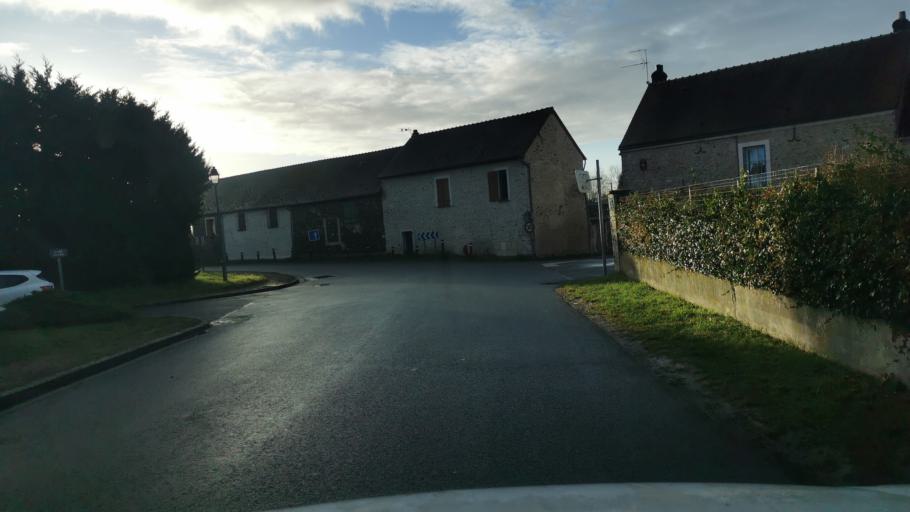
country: FR
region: Ile-de-France
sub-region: Departement des Yvelines
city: Bazainville
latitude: 48.8168
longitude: 1.6370
